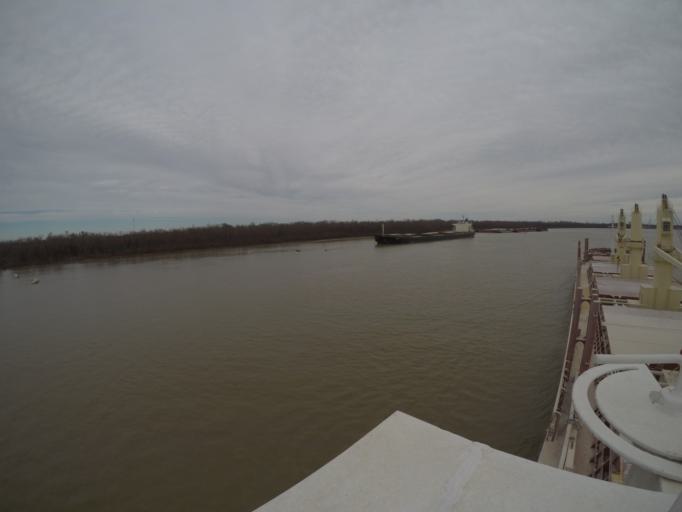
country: US
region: Louisiana
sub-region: Saint John the Baptist Parish
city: Montegut
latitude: 30.0523
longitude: -90.4979
